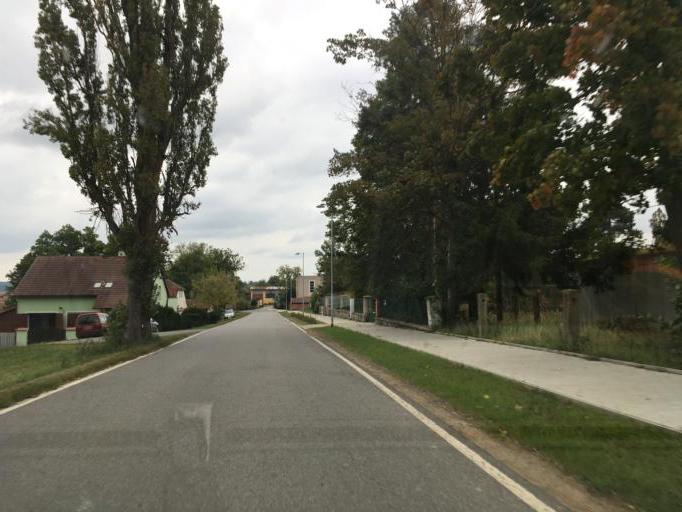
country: CZ
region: Vysocina
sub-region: Okres Jihlava
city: Telc
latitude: 49.1918
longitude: 15.4472
